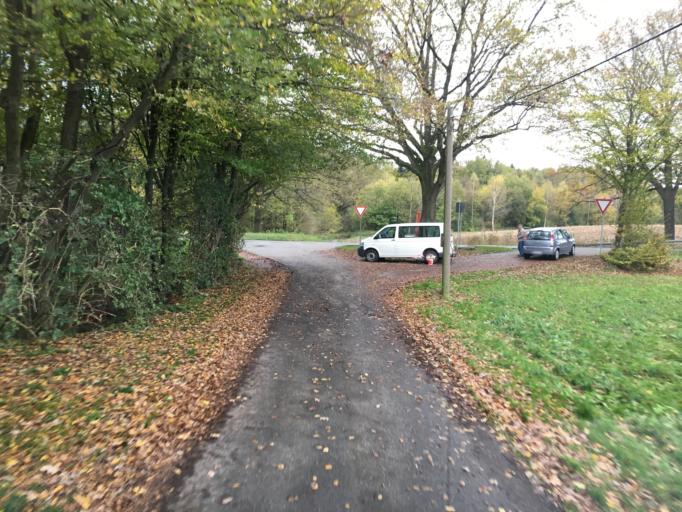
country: DE
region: Saxony
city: Hainichen
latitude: 50.9926
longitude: 13.1177
